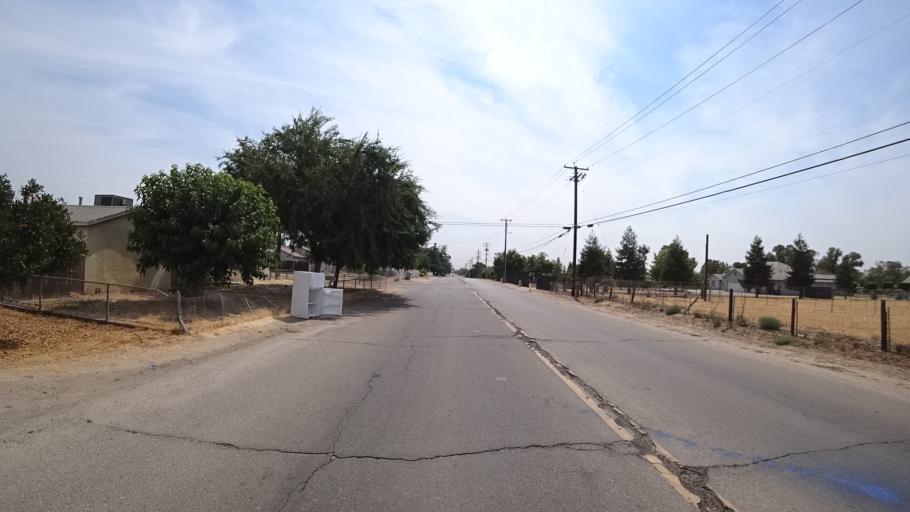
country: US
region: California
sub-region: Fresno County
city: West Park
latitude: 36.7574
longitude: -119.8751
